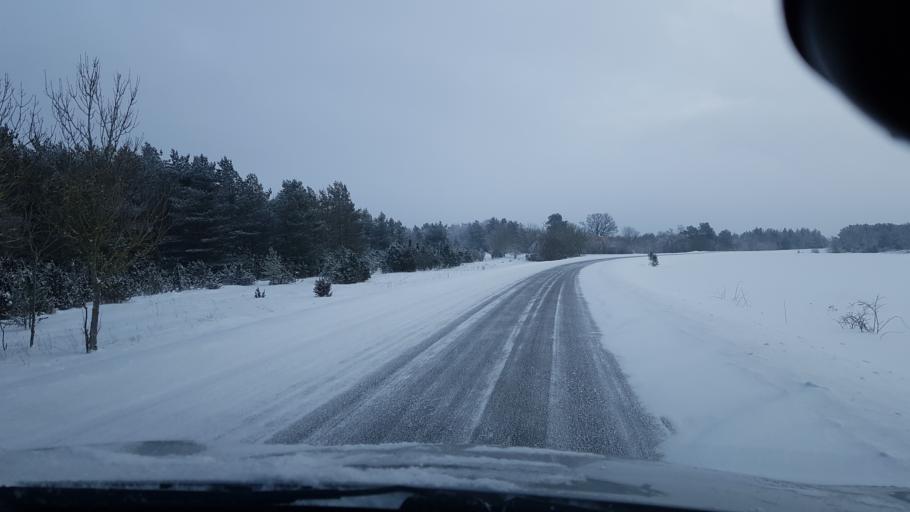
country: EE
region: Harju
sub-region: Keila linn
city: Keila
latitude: 59.3565
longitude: 24.4241
